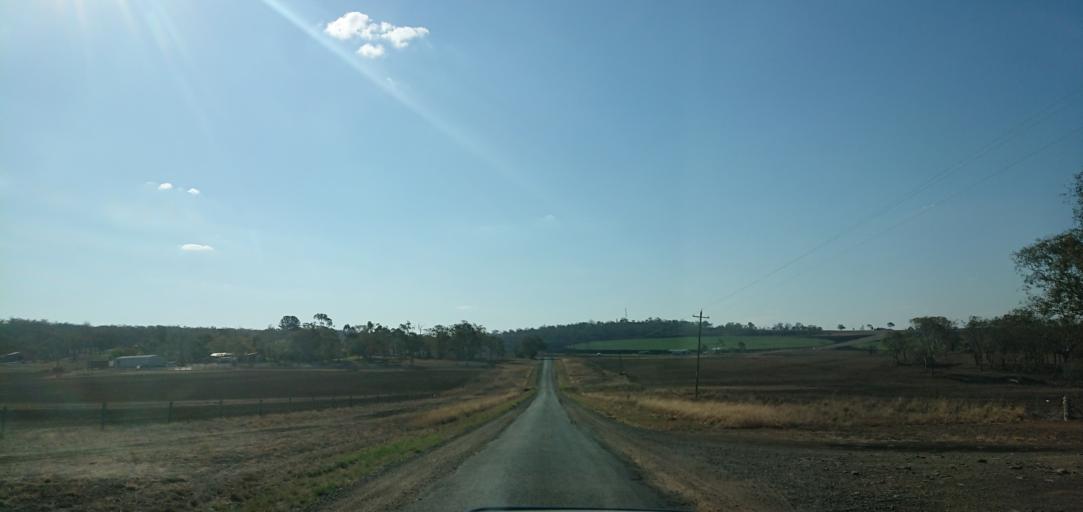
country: AU
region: Queensland
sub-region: Toowoomba
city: Westbrook
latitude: -27.7148
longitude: 151.7189
